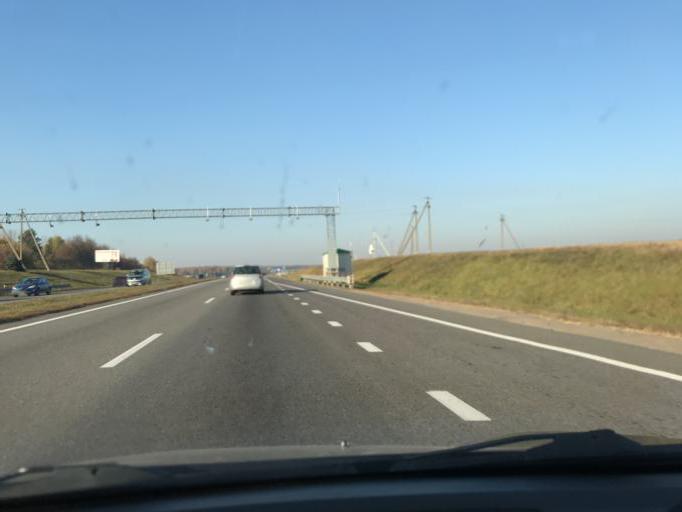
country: BY
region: Minsk
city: Samakhvalavichy
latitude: 53.7329
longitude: 27.5172
